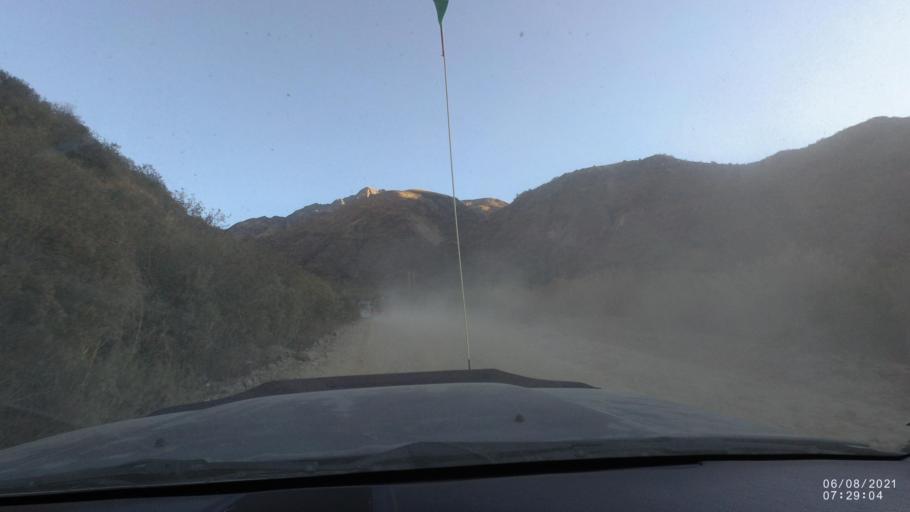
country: BO
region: Cochabamba
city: Sipe Sipe
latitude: -17.2799
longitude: -66.3188
